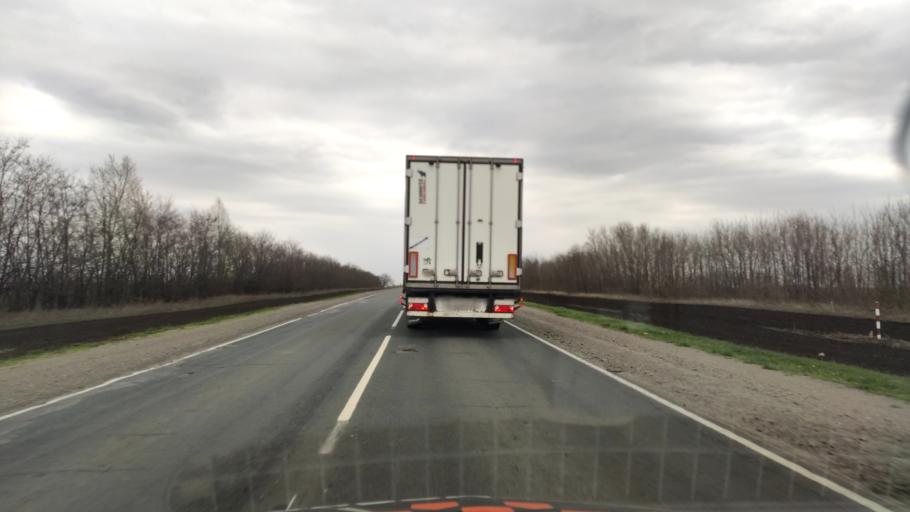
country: RU
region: Voronezj
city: Nizhnedevitsk
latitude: 51.5714
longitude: 38.3330
